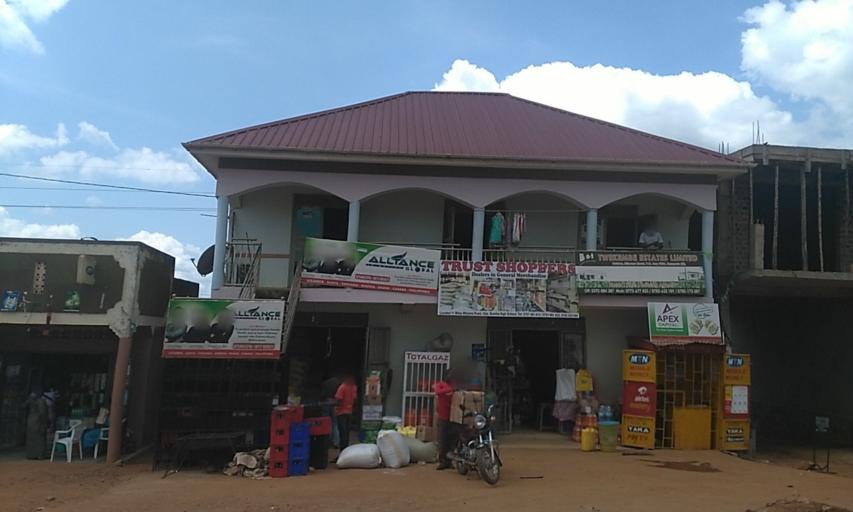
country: UG
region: Central Region
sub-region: Wakiso District
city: Wakiso
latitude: 0.3249
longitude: 32.4584
